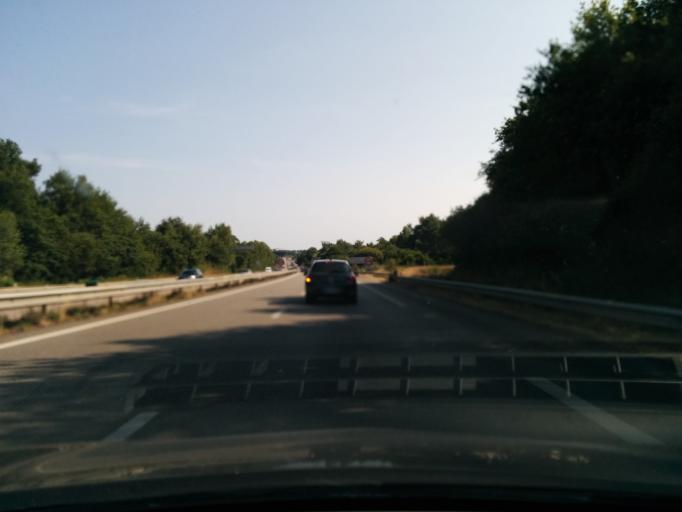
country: FR
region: Limousin
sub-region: Departement de la Haute-Vienne
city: Rilhac-Rancon
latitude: 45.9076
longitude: 1.2916
